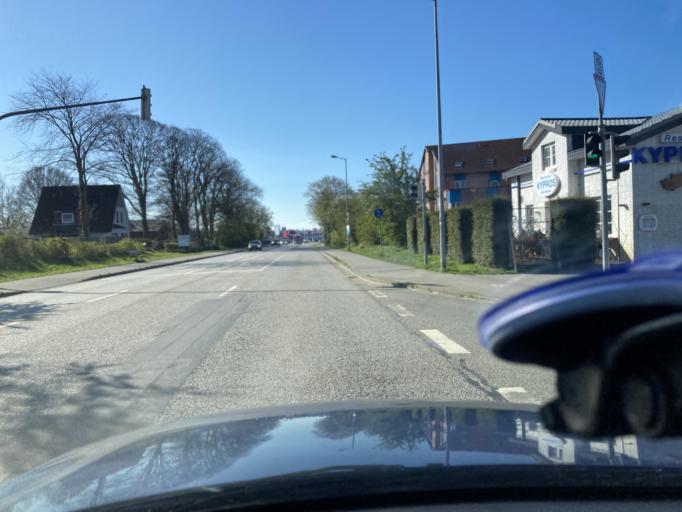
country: DE
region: Schleswig-Holstein
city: Heide
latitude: 54.1800
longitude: 9.0910
